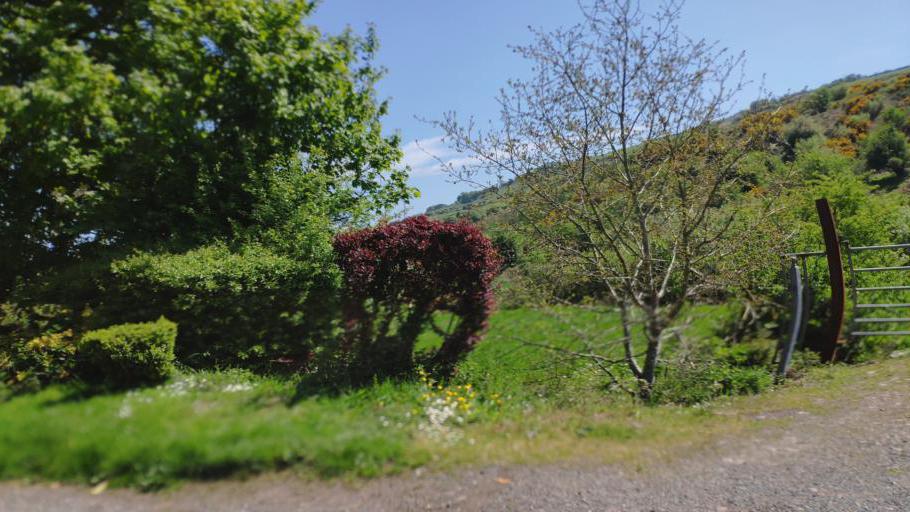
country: IE
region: Munster
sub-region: County Cork
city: Cork
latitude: 51.9167
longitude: -8.5156
